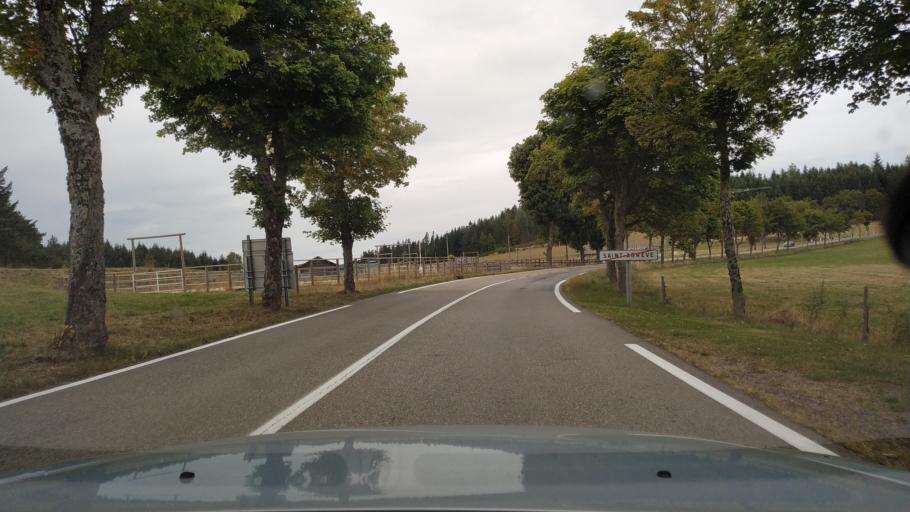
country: FR
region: Rhone-Alpes
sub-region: Departement de l'Ardeche
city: Saint-Agreve
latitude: 45.0147
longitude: 4.4029
